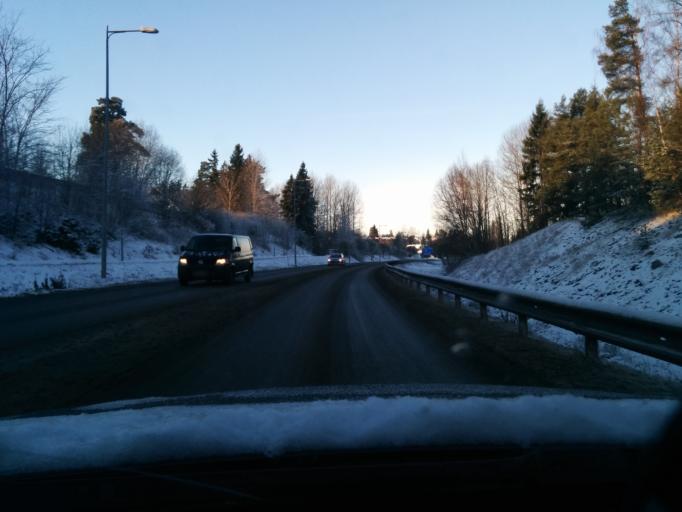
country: SE
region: Stockholm
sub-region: Taby Kommun
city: Taby
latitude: 59.4662
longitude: 18.0594
